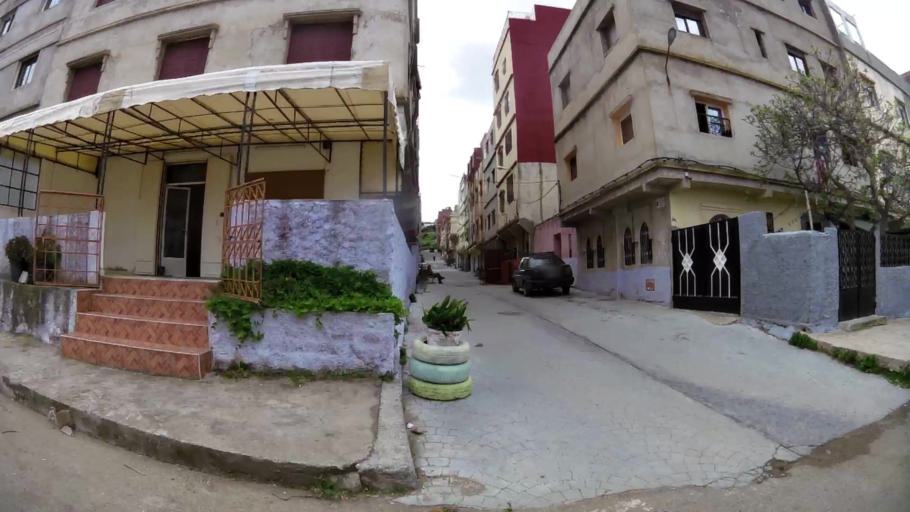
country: MA
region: Tanger-Tetouan
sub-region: Tanger-Assilah
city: Tangier
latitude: 35.7815
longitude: -5.7541
